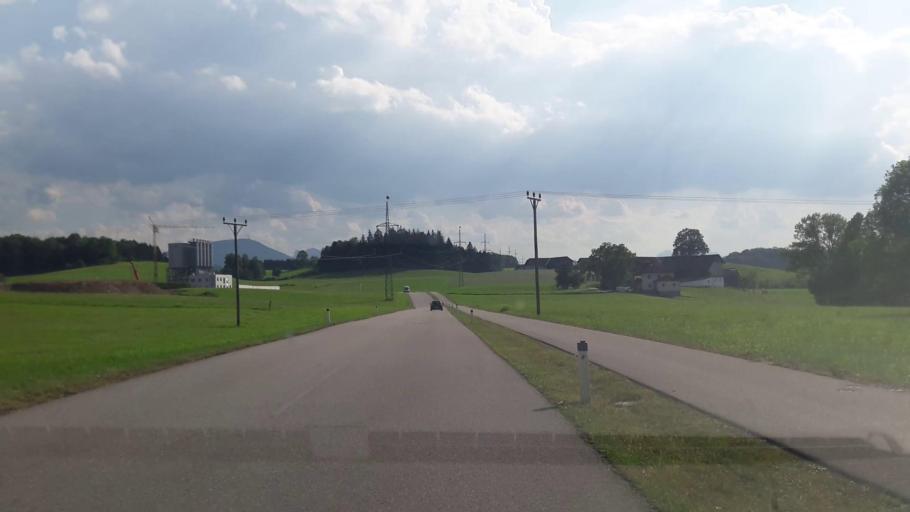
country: AT
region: Salzburg
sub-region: Politischer Bezirk Salzburg-Umgebung
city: Henndorf am Wallersee
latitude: 47.8907
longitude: 13.1912
